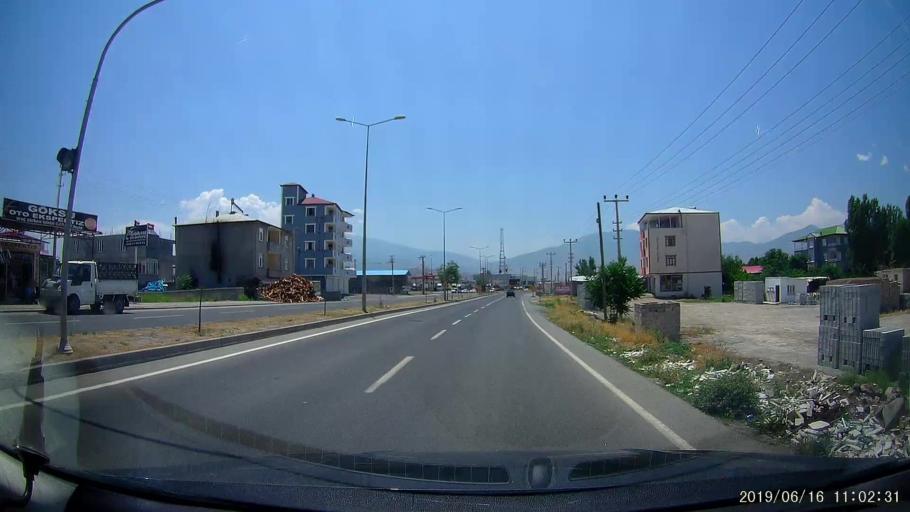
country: TR
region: Igdir
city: Igdir
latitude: 39.9118
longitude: 44.0582
